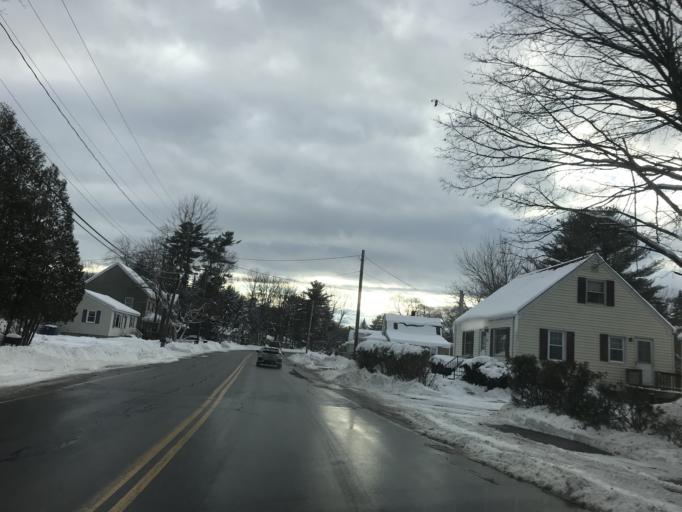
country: US
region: Maine
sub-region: Cumberland County
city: Westbrook
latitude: 43.6951
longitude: -70.3489
